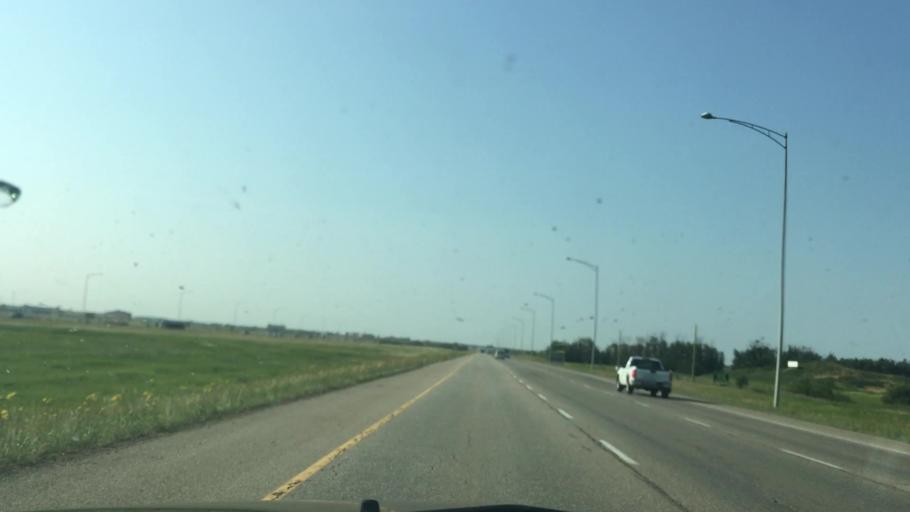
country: CA
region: Alberta
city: Leduc
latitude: 53.3275
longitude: -113.5499
